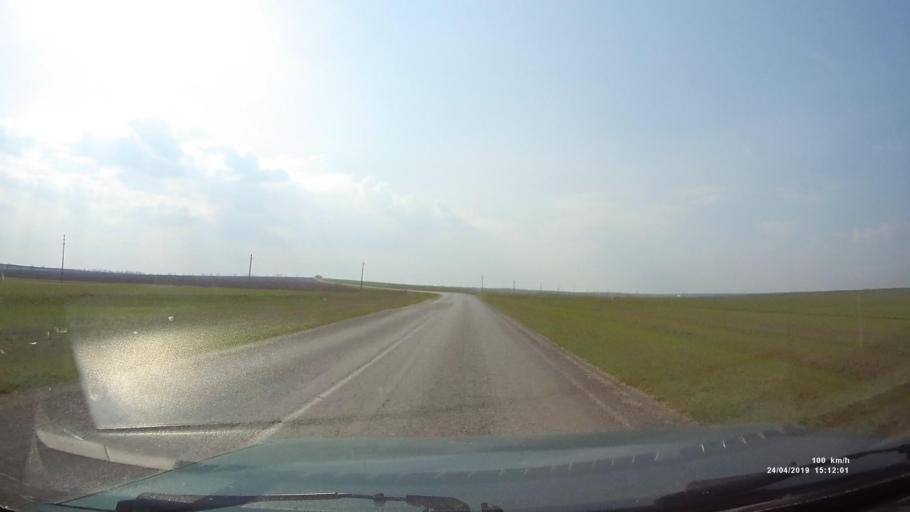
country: RU
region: Rostov
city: Remontnoye
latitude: 46.5459
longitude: 43.3097
